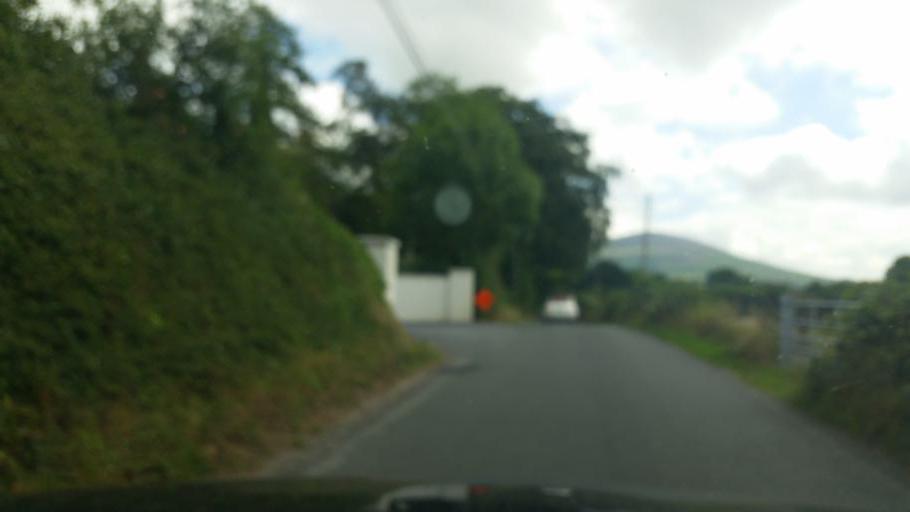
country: IE
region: Leinster
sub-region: Kilkenny
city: Graiguenamanagh
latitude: 52.6133
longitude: -6.8584
